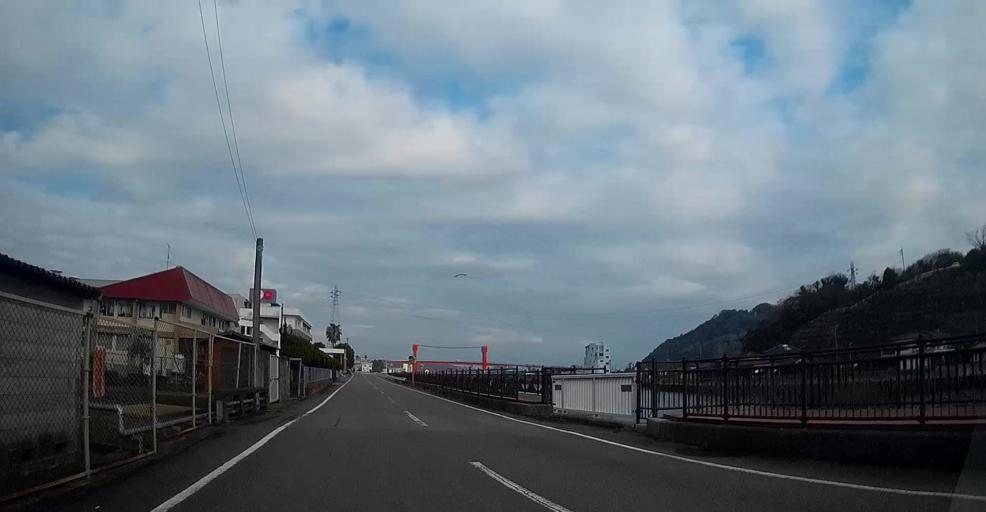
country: JP
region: Kumamoto
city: Hondo
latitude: 32.4415
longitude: 130.2051
